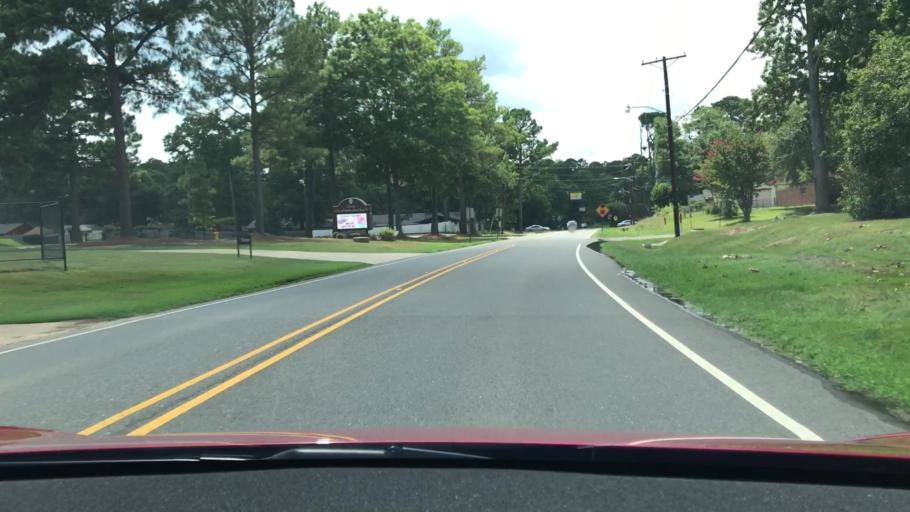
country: US
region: Louisiana
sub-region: De Soto Parish
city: Stonewall
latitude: 32.3891
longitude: -93.7879
